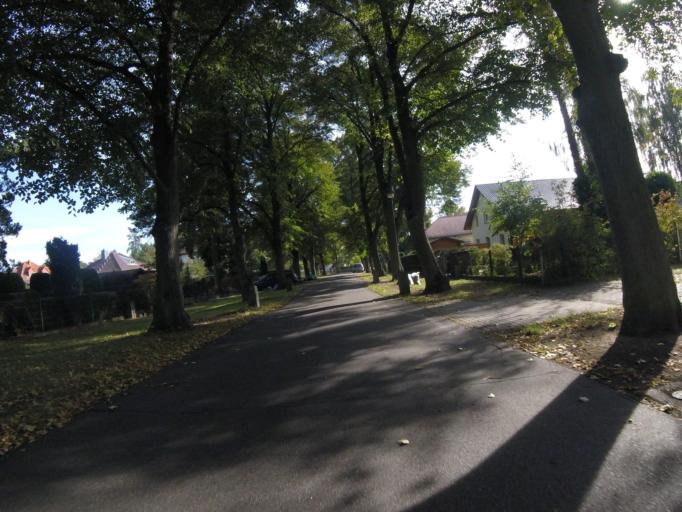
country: DE
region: Brandenburg
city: Konigs Wusterhausen
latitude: 52.2969
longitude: 13.6653
